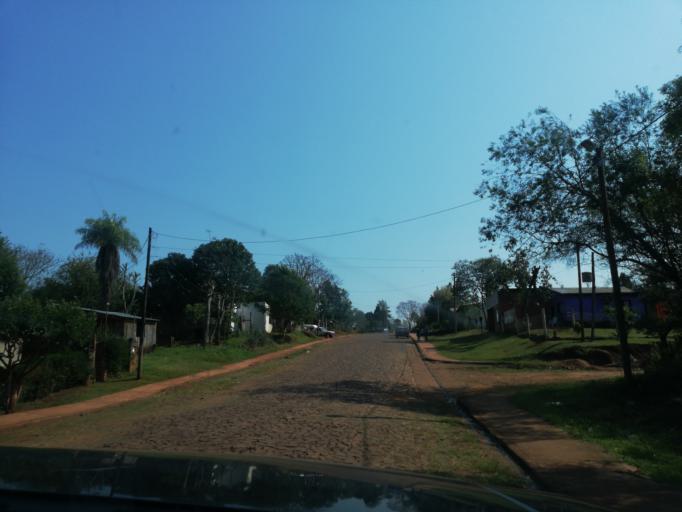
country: AR
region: Misiones
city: Bonpland
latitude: -27.4821
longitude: -55.4817
